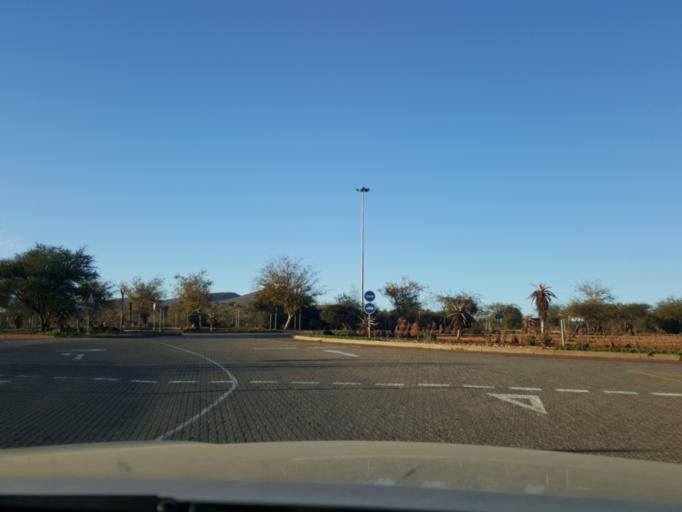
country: BW
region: South East
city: Lobatse
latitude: -25.2770
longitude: 25.7139
